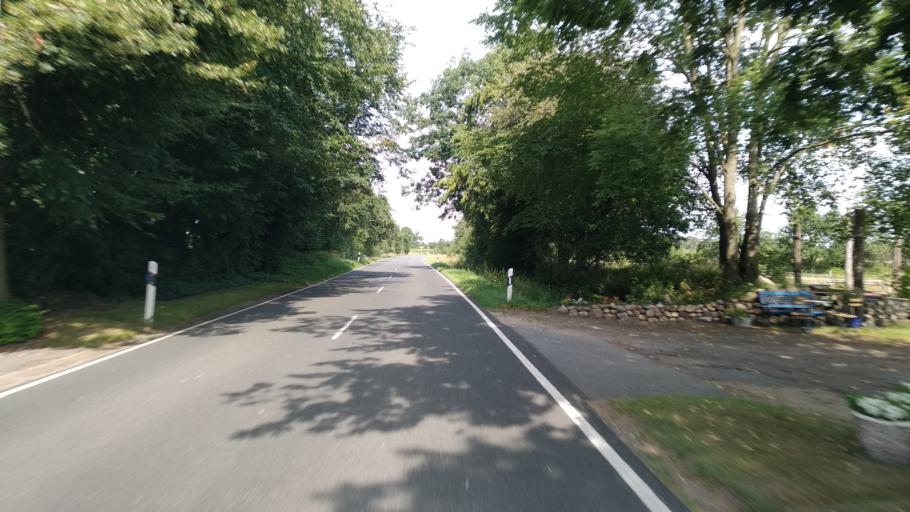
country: DE
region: Schleswig-Holstein
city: Lottorf
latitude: 54.4575
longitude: 9.5853
